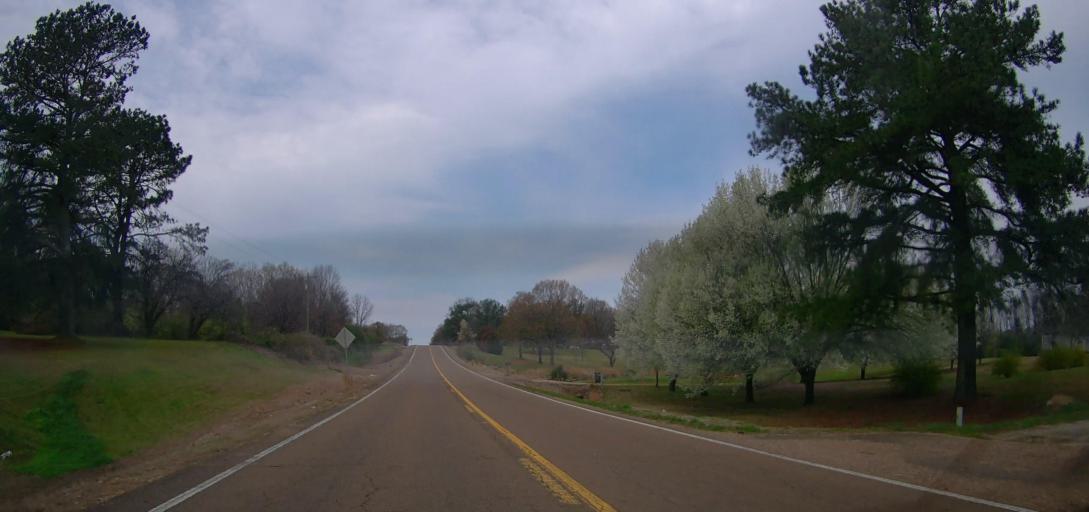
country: US
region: Mississippi
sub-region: Marshall County
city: Byhalia
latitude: 34.8414
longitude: -89.6037
